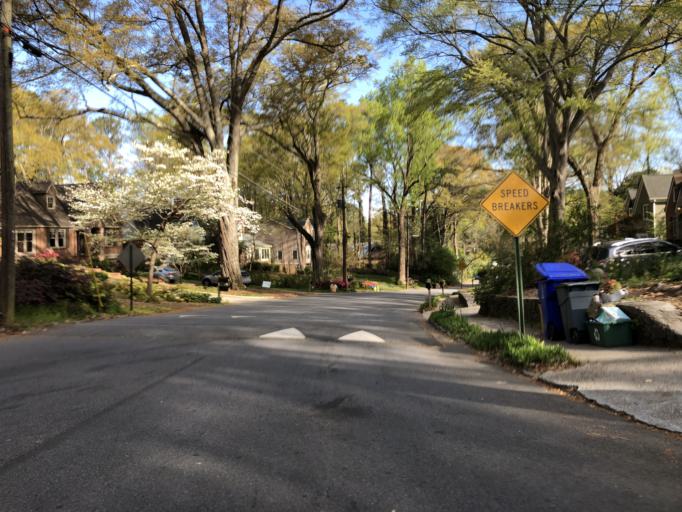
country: US
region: Georgia
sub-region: DeKalb County
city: North Decatur
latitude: 33.7883
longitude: -84.2996
